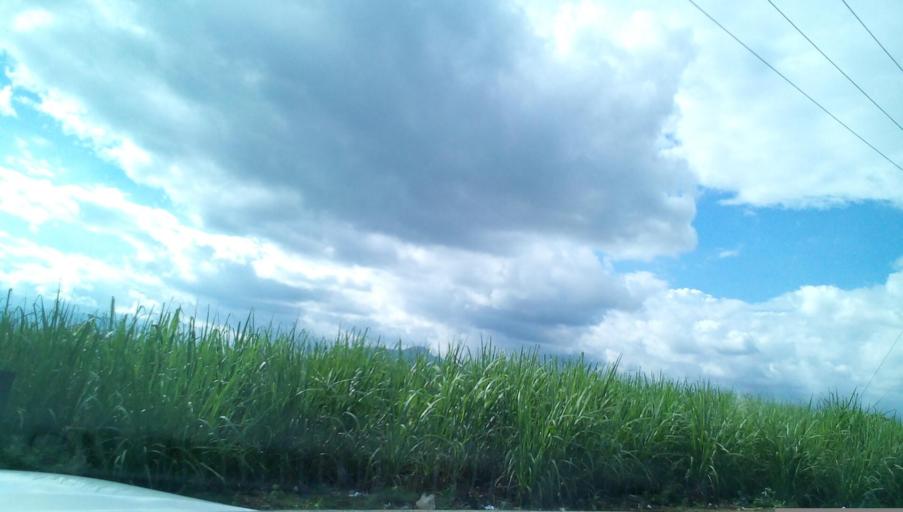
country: MX
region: Veracruz
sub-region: Amatlan de los Reyes
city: Centro de Readaptacion Social
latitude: 18.8248
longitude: -96.9241
